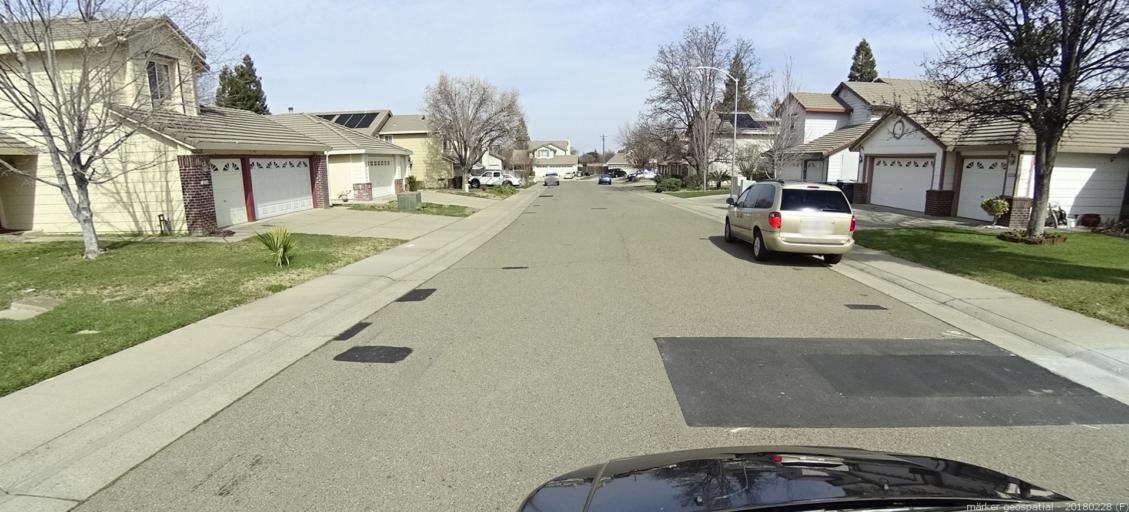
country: US
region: California
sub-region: Sacramento County
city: Antelope
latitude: 38.7239
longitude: -121.3434
